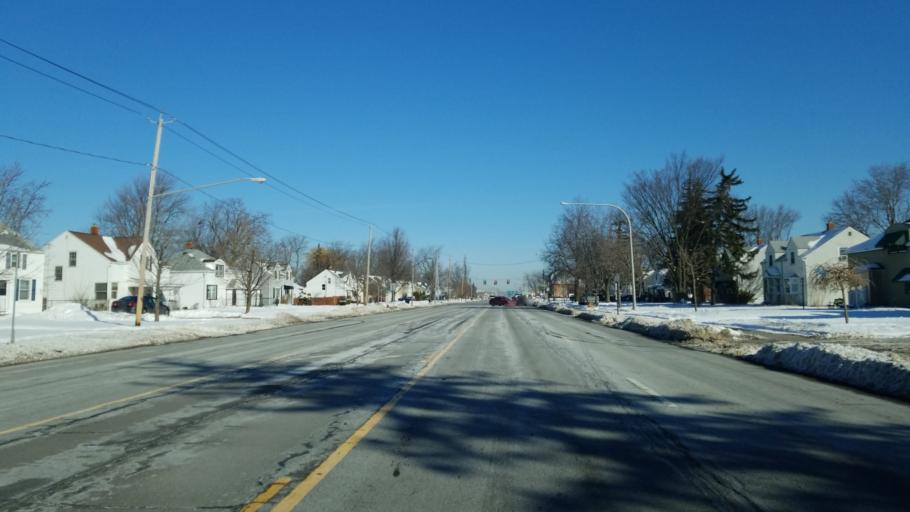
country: US
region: New York
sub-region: Erie County
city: Eggertsville
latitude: 42.9707
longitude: -78.8233
